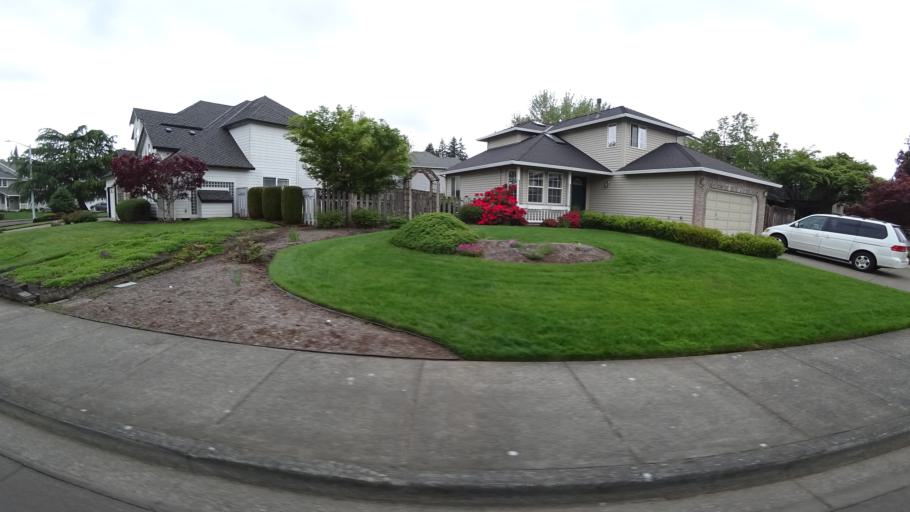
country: US
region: Oregon
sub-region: Washington County
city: Hillsboro
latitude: 45.5421
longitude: -122.9854
